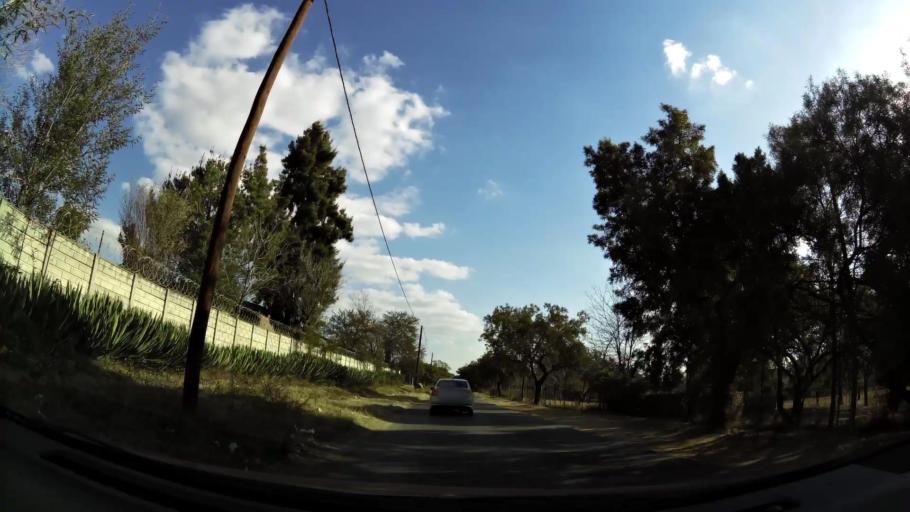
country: ZA
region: Gauteng
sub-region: City of Johannesburg Metropolitan Municipality
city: Midrand
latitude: -26.0202
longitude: 28.1481
